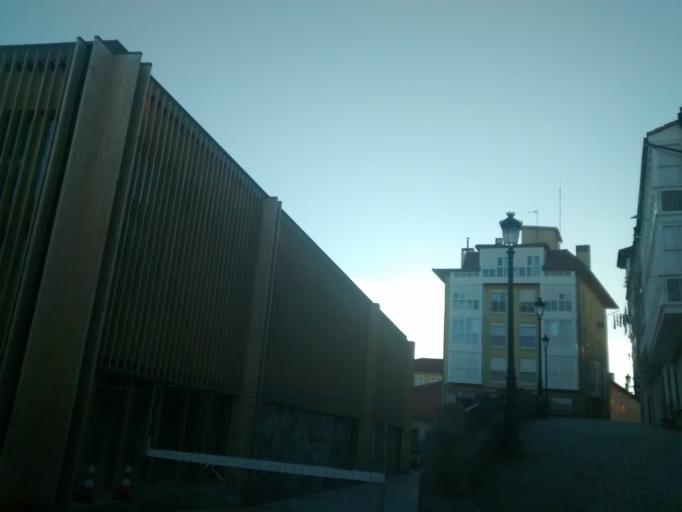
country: ES
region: Cantabria
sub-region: Provincia de Cantabria
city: Reinosa
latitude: 43.0025
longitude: -4.1373
